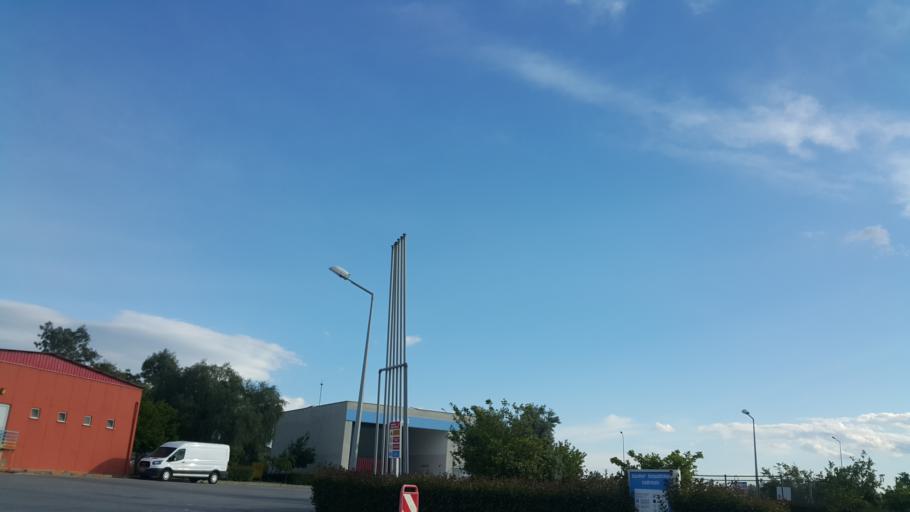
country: TR
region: Hatay
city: Mahmutlar
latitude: 36.9530
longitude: 36.1590
